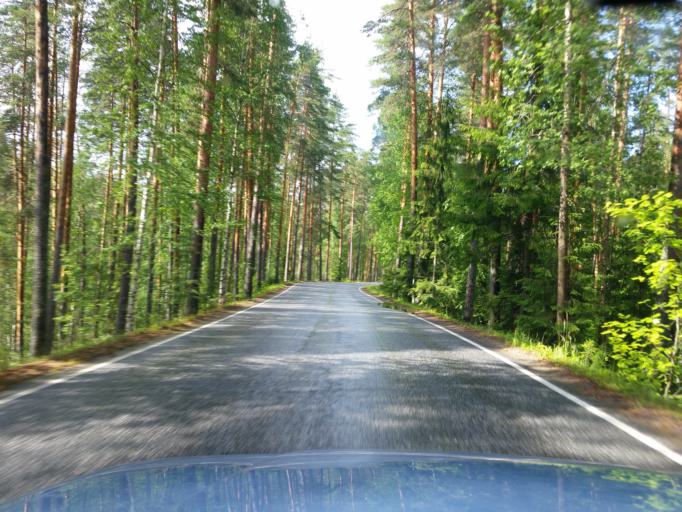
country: FI
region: Southern Savonia
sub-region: Savonlinna
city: Sulkava
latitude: 61.7897
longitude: 28.4247
